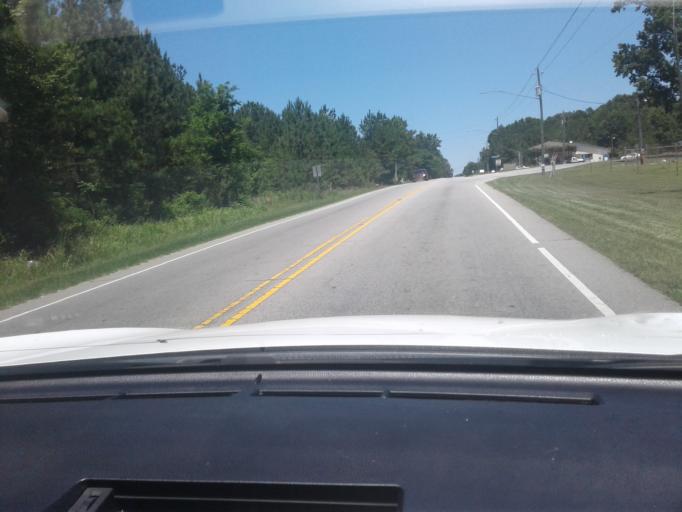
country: US
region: North Carolina
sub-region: Harnett County
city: Erwin
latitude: 35.3147
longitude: -78.6860
